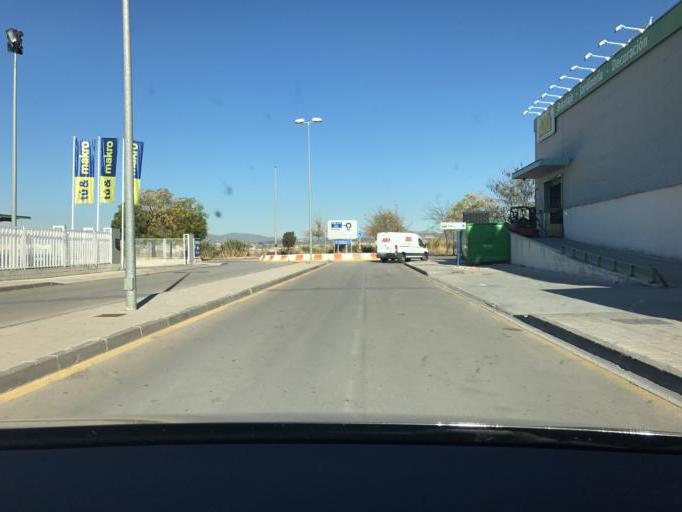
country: ES
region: Andalusia
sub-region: Provincia de Granada
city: Pulianas
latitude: 37.2148
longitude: -3.6193
